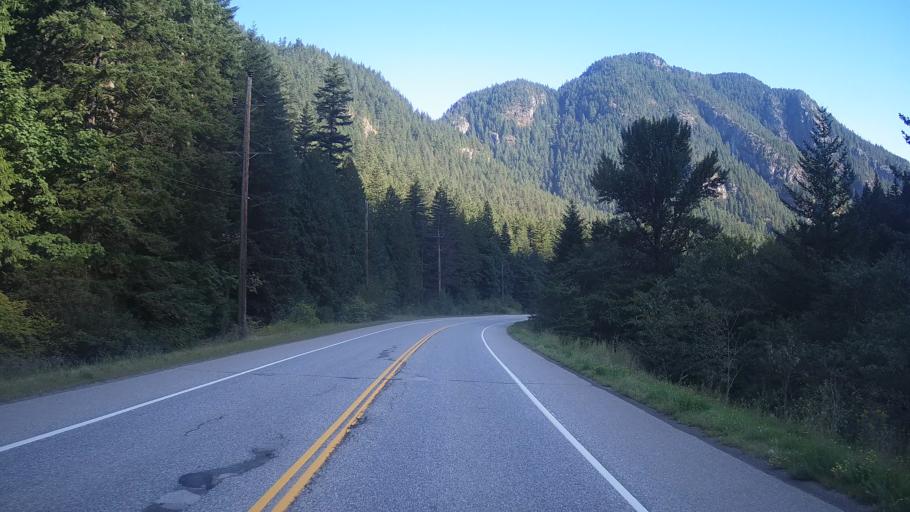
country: CA
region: British Columbia
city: Hope
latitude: 49.5995
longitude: -121.4151
